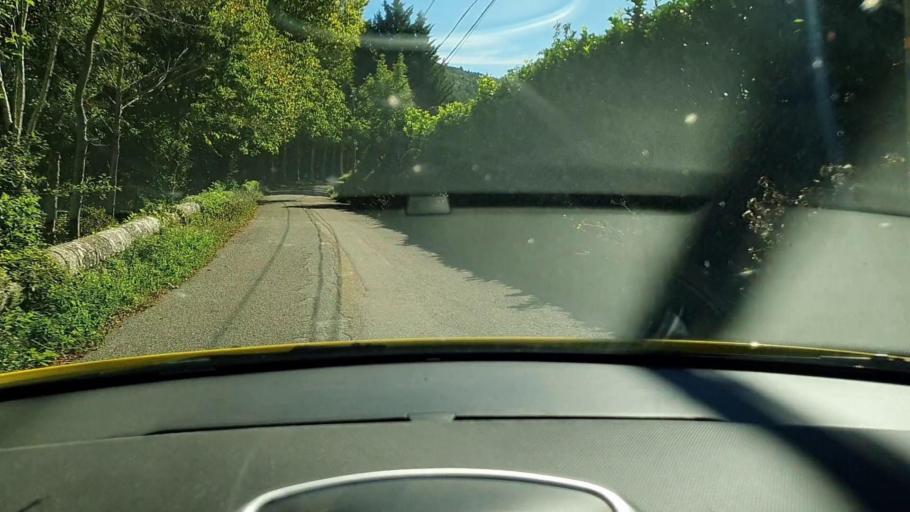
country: FR
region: Languedoc-Roussillon
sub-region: Departement du Gard
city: Le Vigan
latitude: 43.9702
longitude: 3.4375
